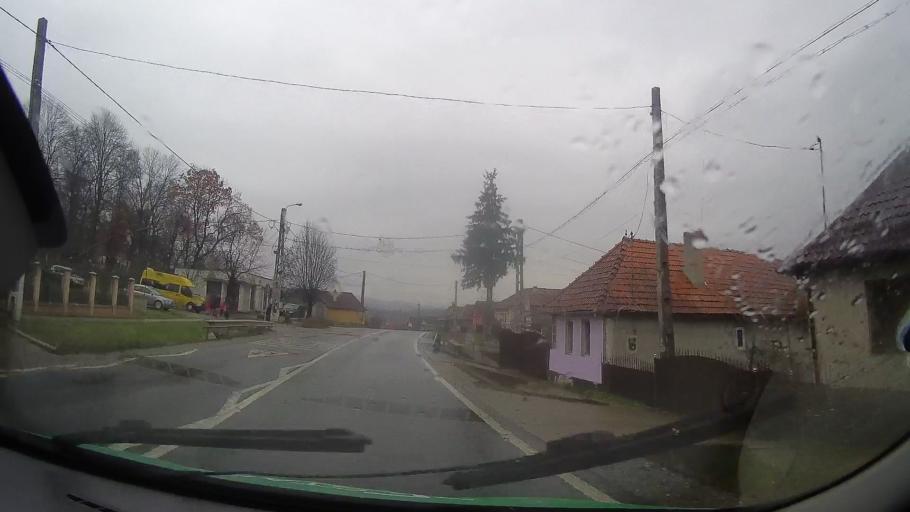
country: RO
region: Bistrita-Nasaud
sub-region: Comuna Galatii Bistritei
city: Galatii Bistritei
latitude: 46.9918
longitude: 24.4215
